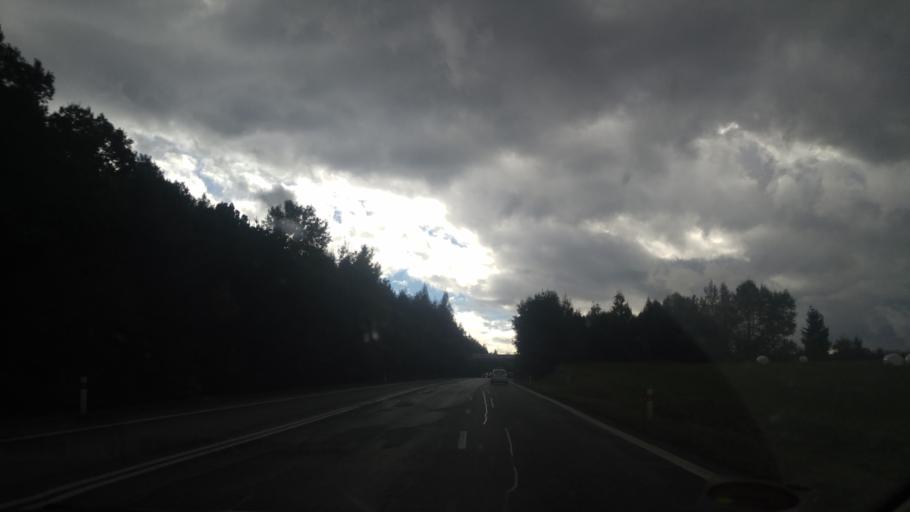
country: CZ
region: Jihocesky
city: Sevetin
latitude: 49.0865
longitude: 14.5565
